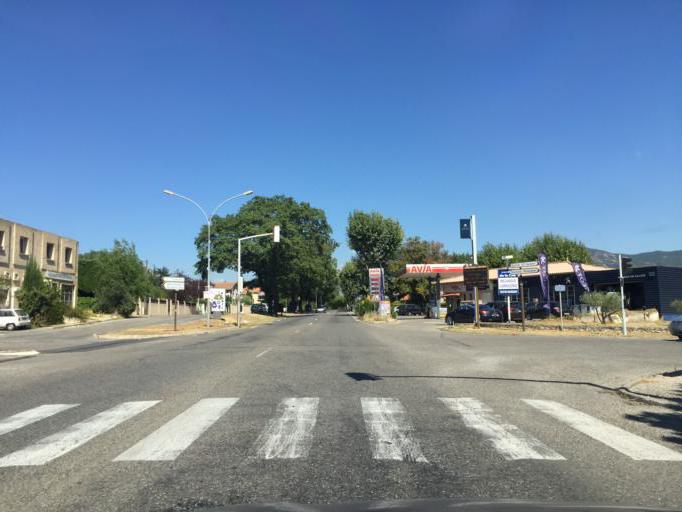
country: FR
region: Provence-Alpes-Cote d'Azur
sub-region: Departement des Alpes-de-Haute-Provence
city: Volonne
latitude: 44.0743
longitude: 5.9920
